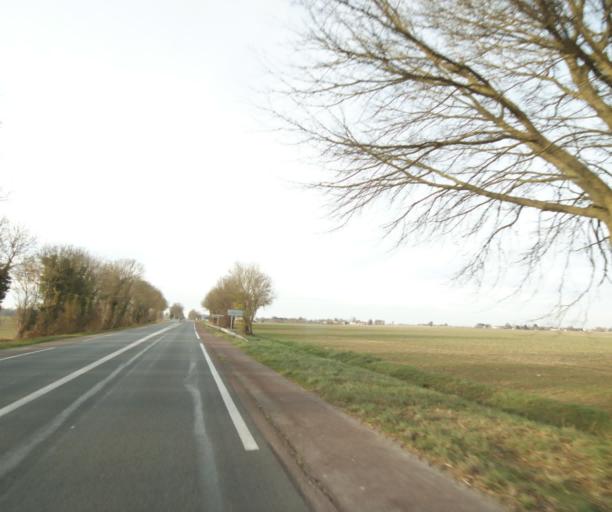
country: FR
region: Poitou-Charentes
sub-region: Departement de la Charente-Maritime
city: Nieul-les-Saintes
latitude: 45.7987
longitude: -0.7410
